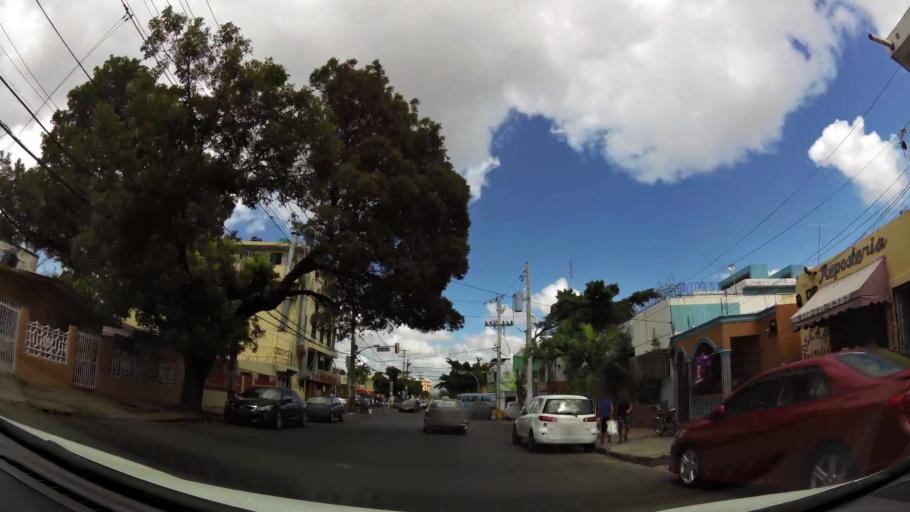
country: DO
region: Nacional
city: Ensanche Luperon
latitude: 18.5017
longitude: -69.8945
